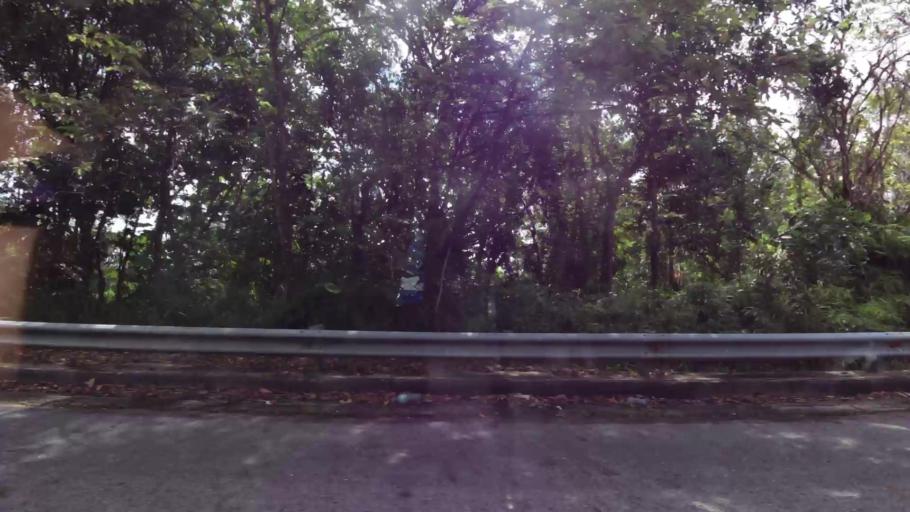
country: BN
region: Brunei and Muara
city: Bandar Seri Begawan
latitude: 4.9326
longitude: 114.9047
